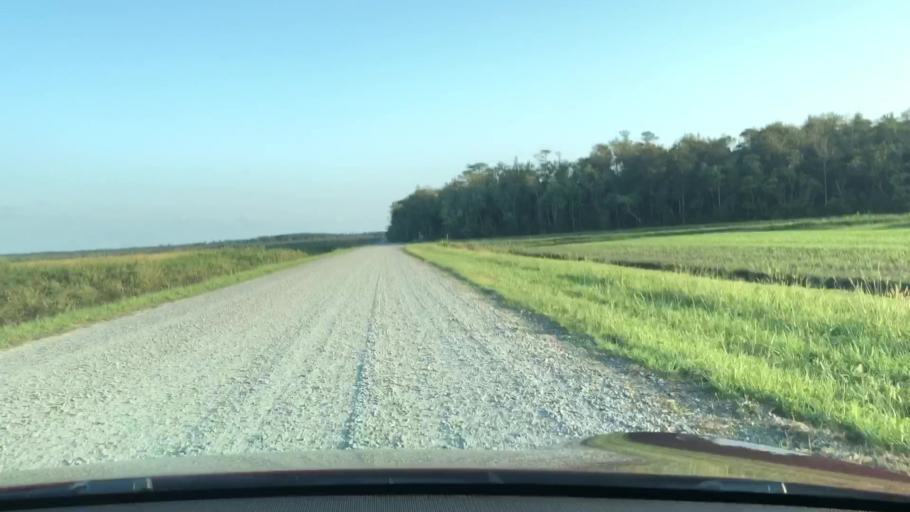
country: US
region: North Carolina
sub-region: Dare County
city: Manteo
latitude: 35.8461
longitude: -75.8607
